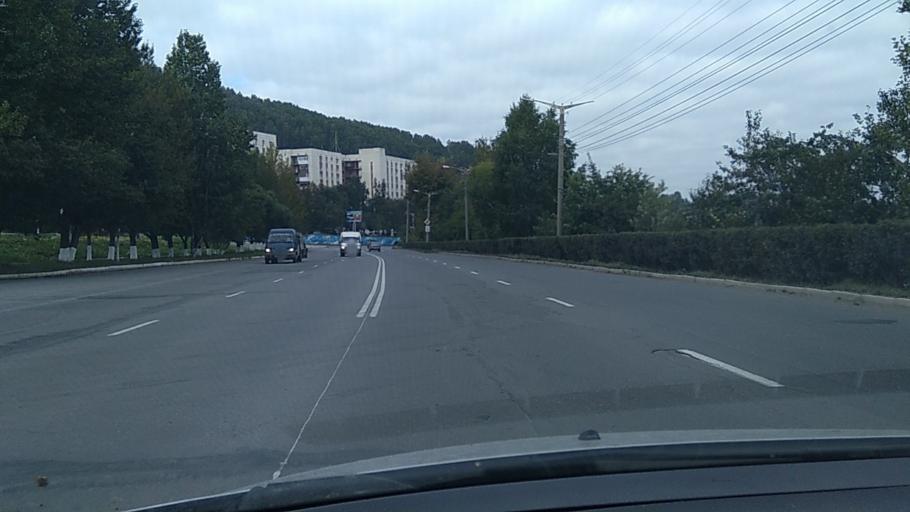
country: RU
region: Chelyabinsk
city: Zlatoust
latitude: 55.1687
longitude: 59.6776
